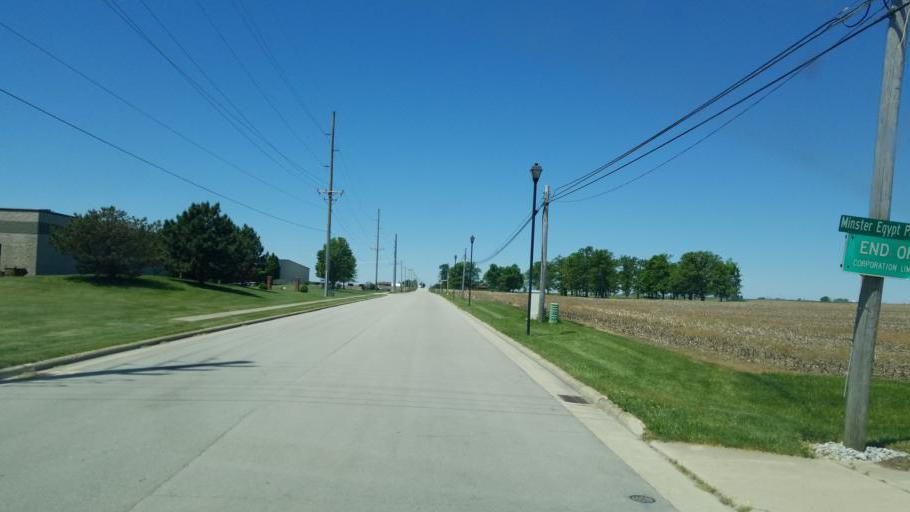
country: US
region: Ohio
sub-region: Auglaize County
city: Minster
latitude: 40.3856
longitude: -84.3879
